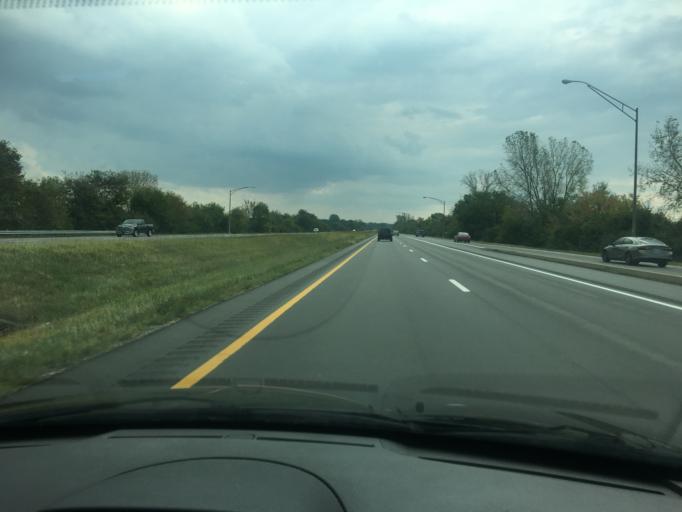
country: US
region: Ohio
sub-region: Clark County
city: Northridge
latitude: 39.9834
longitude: -83.8142
